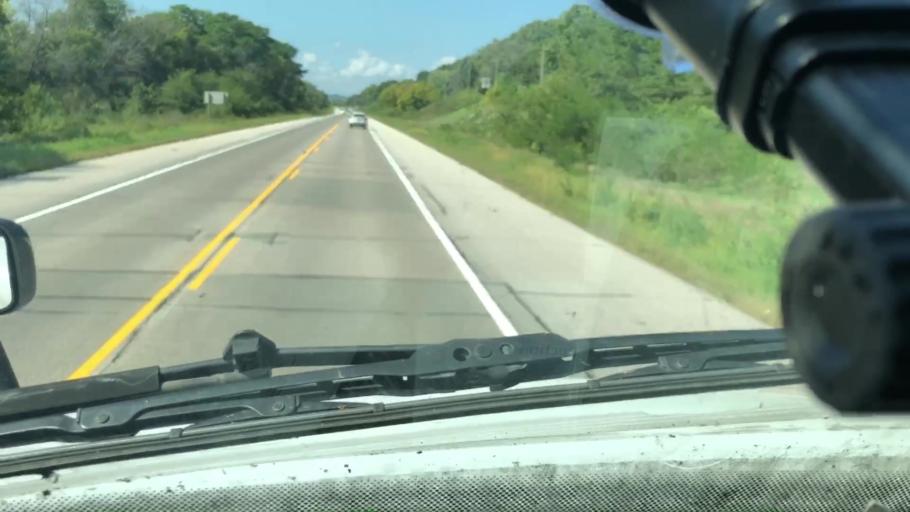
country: US
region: Minnesota
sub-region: Winona County
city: Winona
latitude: 44.0702
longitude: -91.6056
